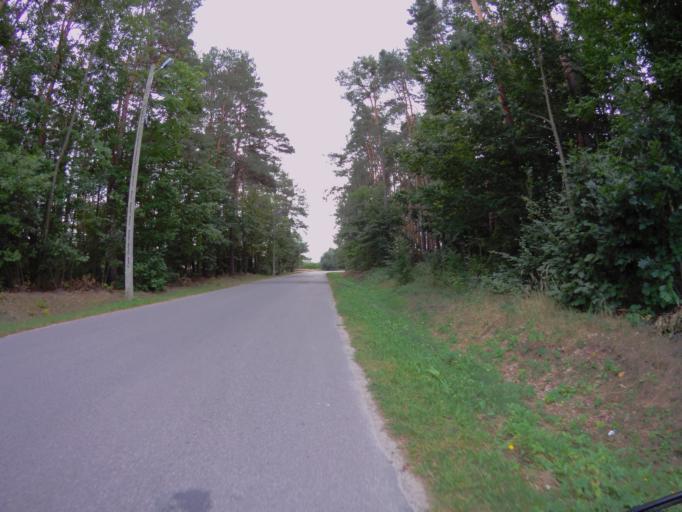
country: PL
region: Subcarpathian Voivodeship
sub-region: Powiat lezajski
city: Brzoza Krolewska
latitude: 50.2428
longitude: 22.3221
